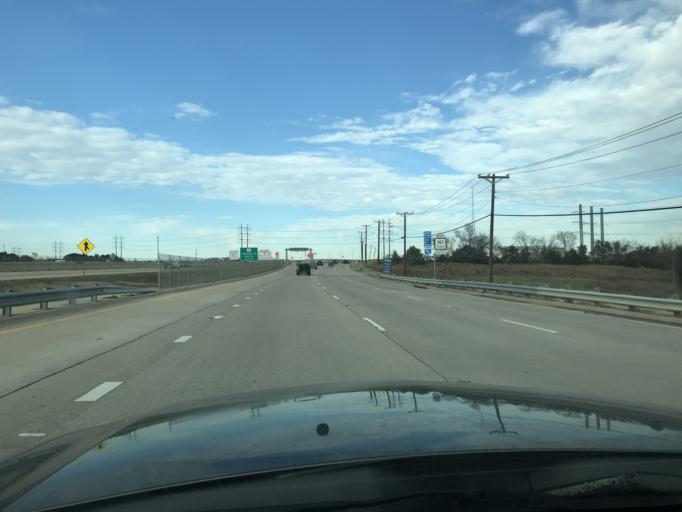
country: US
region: Texas
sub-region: Dallas County
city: Grand Prairie
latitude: 32.7153
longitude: -97.0240
